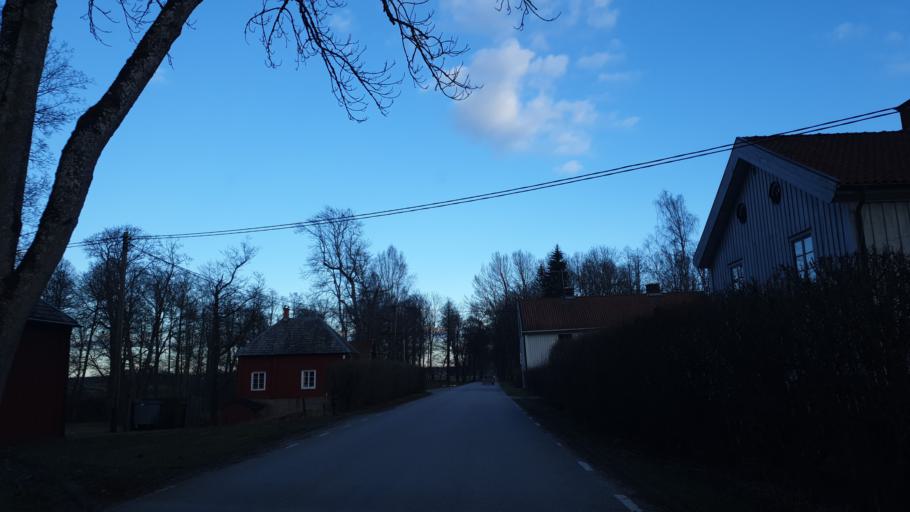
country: SE
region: OErebro
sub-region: Orebro Kommun
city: Garphyttan
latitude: 59.3434
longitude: 15.0120
